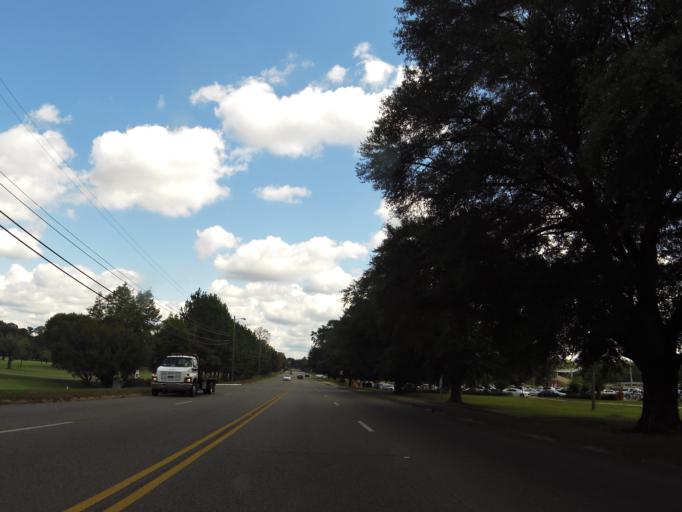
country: US
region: Alabama
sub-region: Dallas County
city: Selma
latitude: 32.4058
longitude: -87.0421
